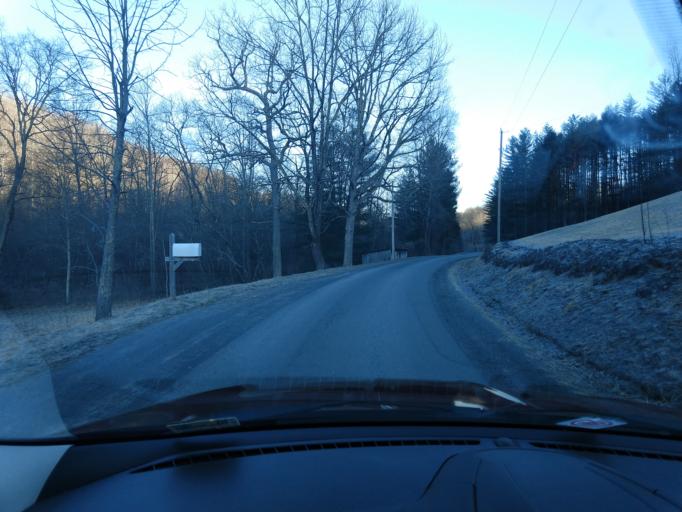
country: US
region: West Virginia
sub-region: Greenbrier County
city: Rainelle
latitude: 37.8867
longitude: -80.7276
